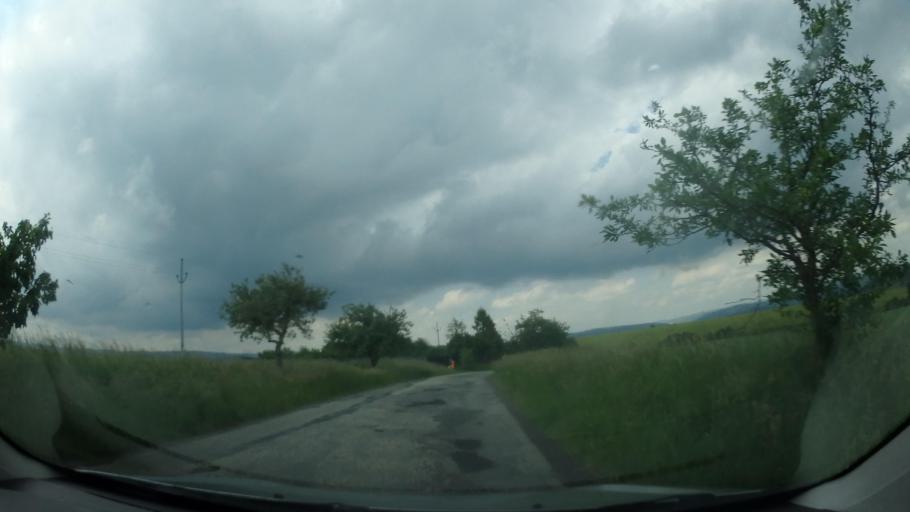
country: CZ
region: South Moravian
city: Boritov
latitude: 49.4565
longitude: 16.5976
